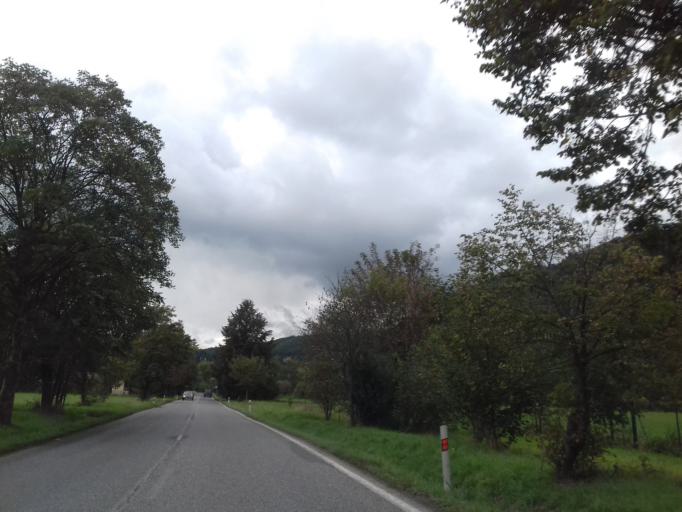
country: CZ
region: Central Bohemia
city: Cernosice
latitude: 49.9695
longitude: 14.3362
